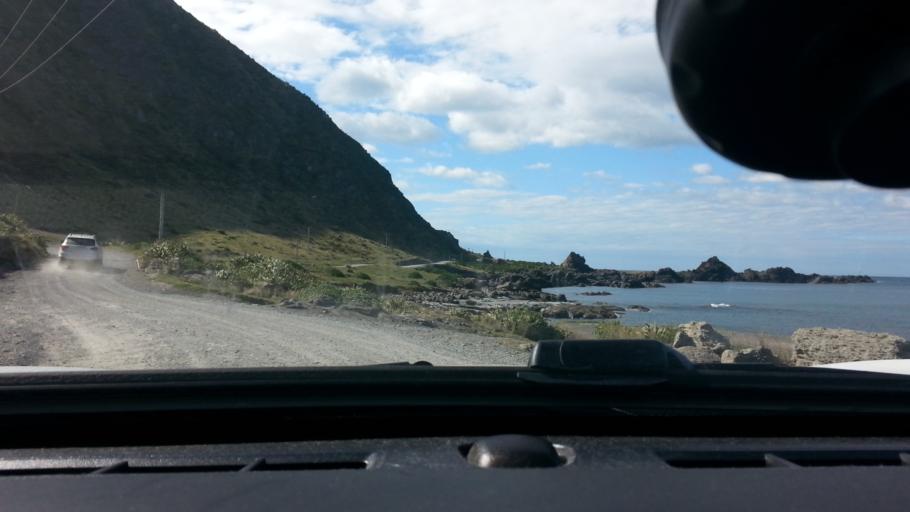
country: NZ
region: Wellington
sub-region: South Wairarapa District
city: Waipawa
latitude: -41.6058
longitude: 175.2659
